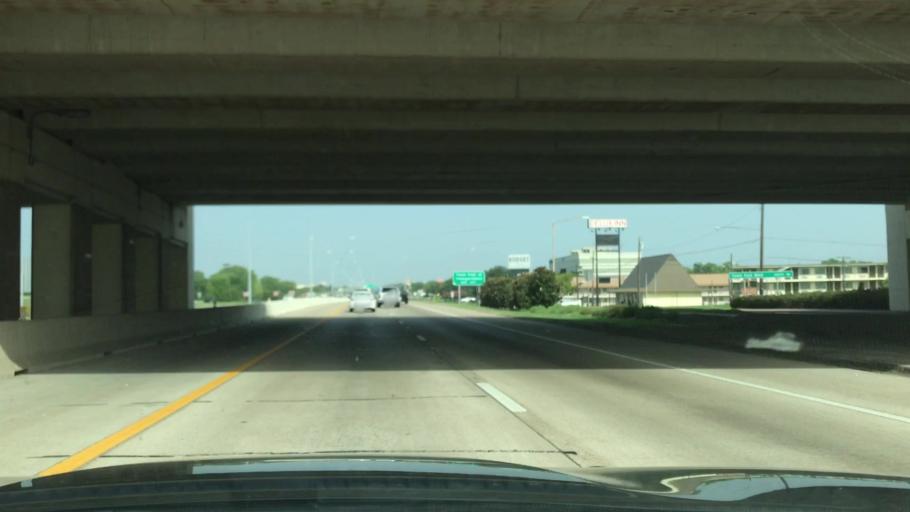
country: US
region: Texas
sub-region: Dallas County
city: Mesquite
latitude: 32.7933
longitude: -96.6555
